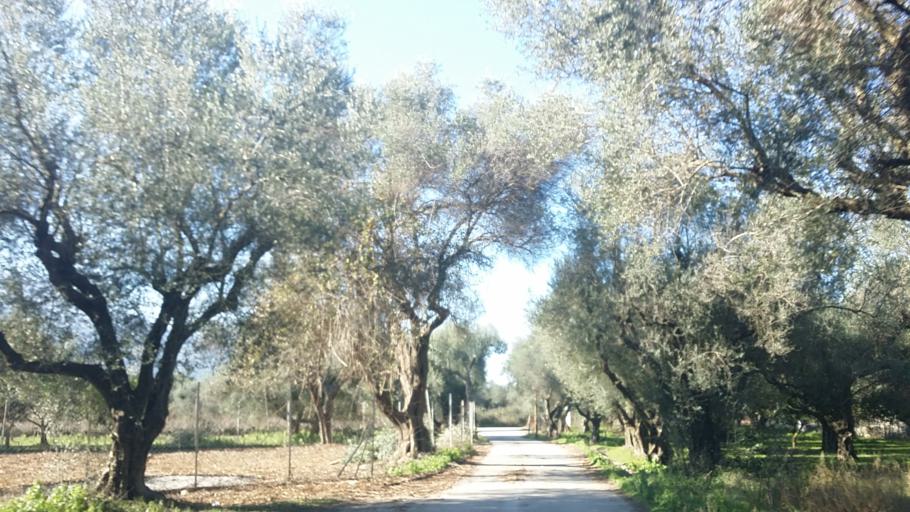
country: GR
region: West Greece
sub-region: Nomos Achaias
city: Temeni
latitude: 38.1962
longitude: 22.1810
